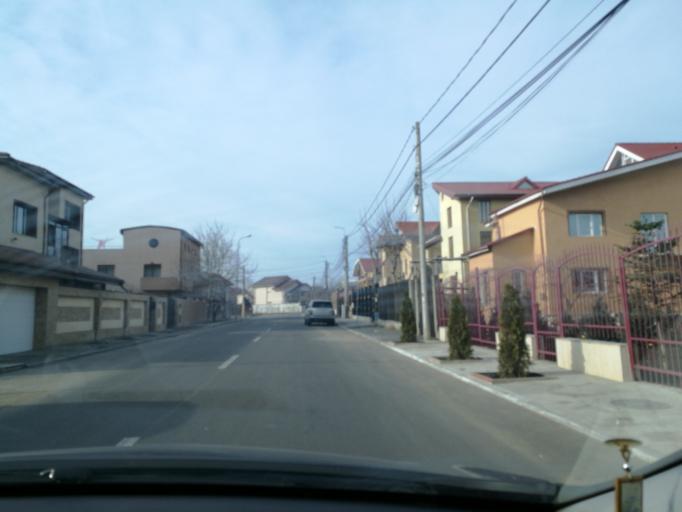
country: RO
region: Constanta
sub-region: Municipiul Constanta
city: Constanta
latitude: 44.1802
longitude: 28.6131
